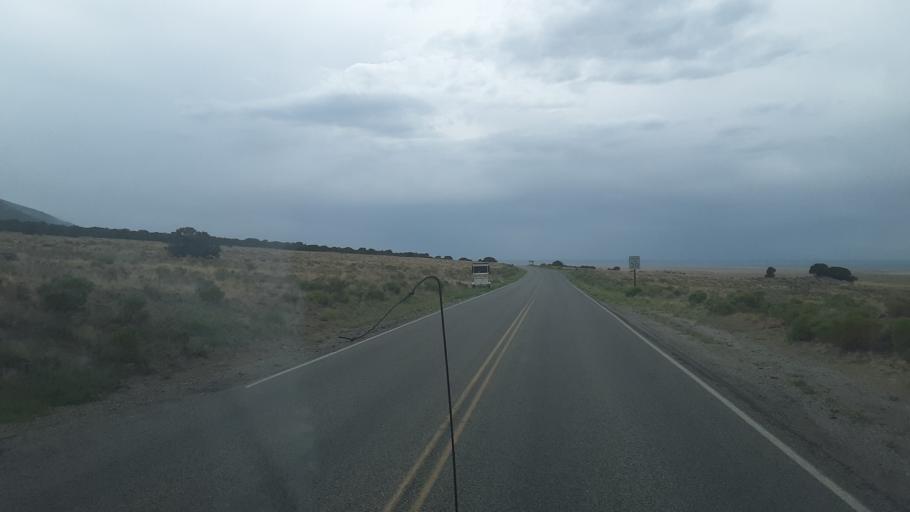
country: US
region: Colorado
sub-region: Custer County
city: Westcliffe
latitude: 37.7318
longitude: -105.5121
